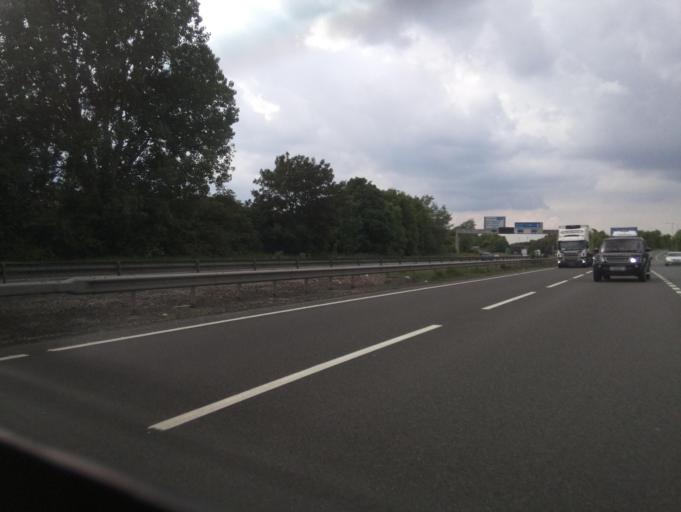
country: GB
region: England
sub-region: North Yorkshire
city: Boroughbridge
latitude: 54.1557
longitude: -1.4217
